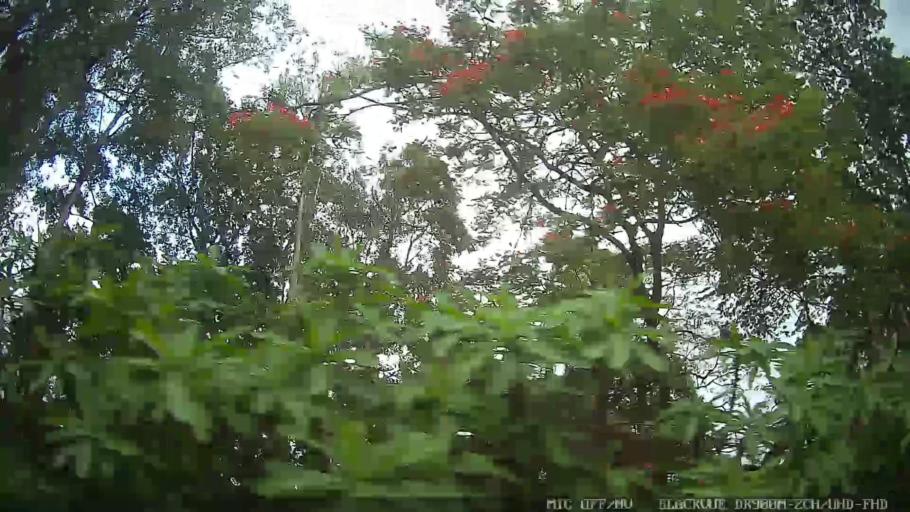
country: BR
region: Sao Paulo
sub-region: Jaguariuna
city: Jaguariuna
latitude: -22.7420
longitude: -47.0068
